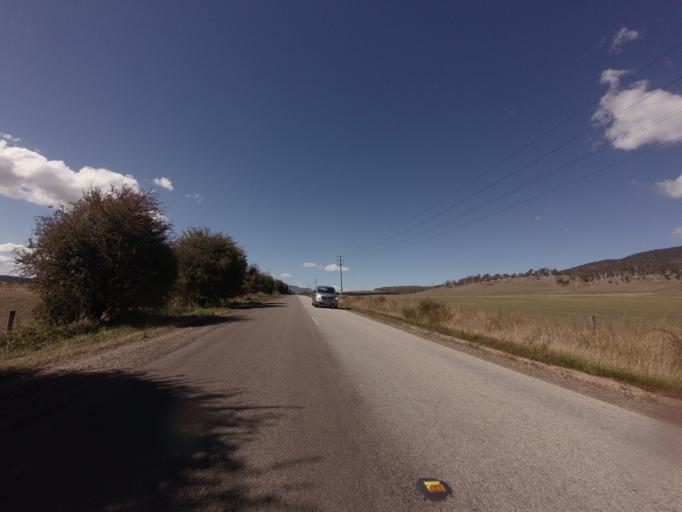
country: AU
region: Tasmania
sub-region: Break O'Day
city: St Helens
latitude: -41.6256
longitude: 147.9938
